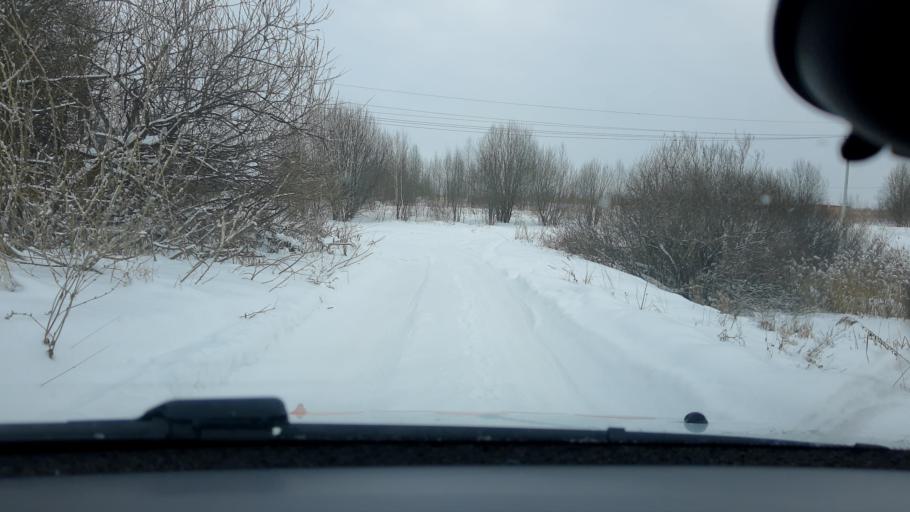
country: RU
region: Nizjnij Novgorod
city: Afonino
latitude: 56.1978
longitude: 44.0989
